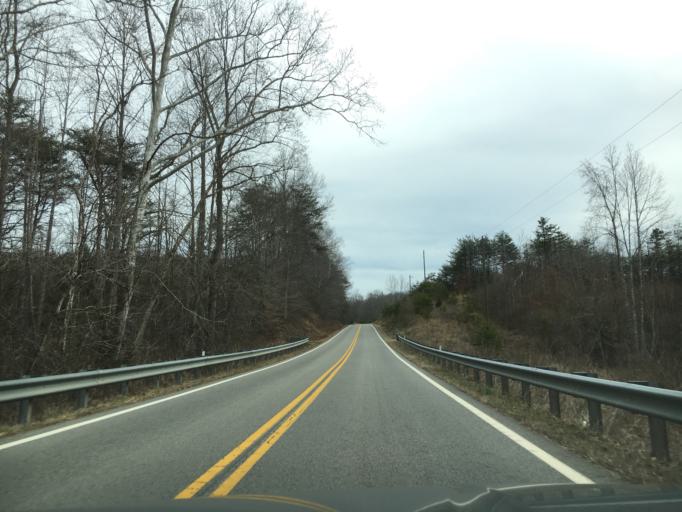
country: US
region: Virginia
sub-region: Charlotte County
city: Charlotte Court House
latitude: 37.1511
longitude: -78.7630
